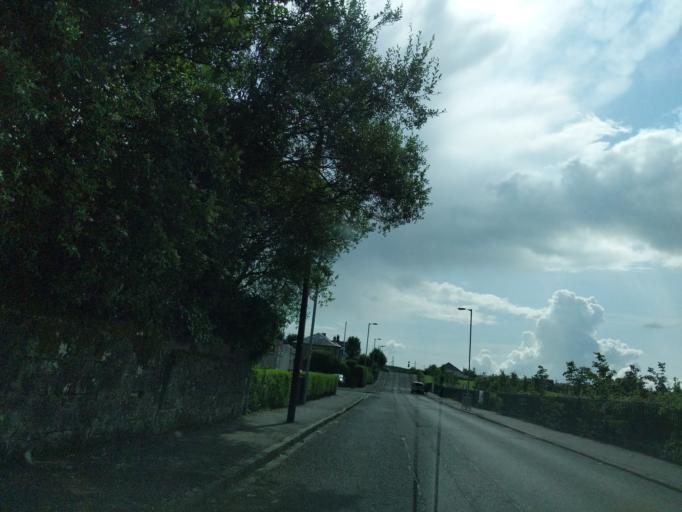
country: GB
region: Scotland
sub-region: East Renfrewshire
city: Neilston
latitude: 55.7822
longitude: -4.4263
